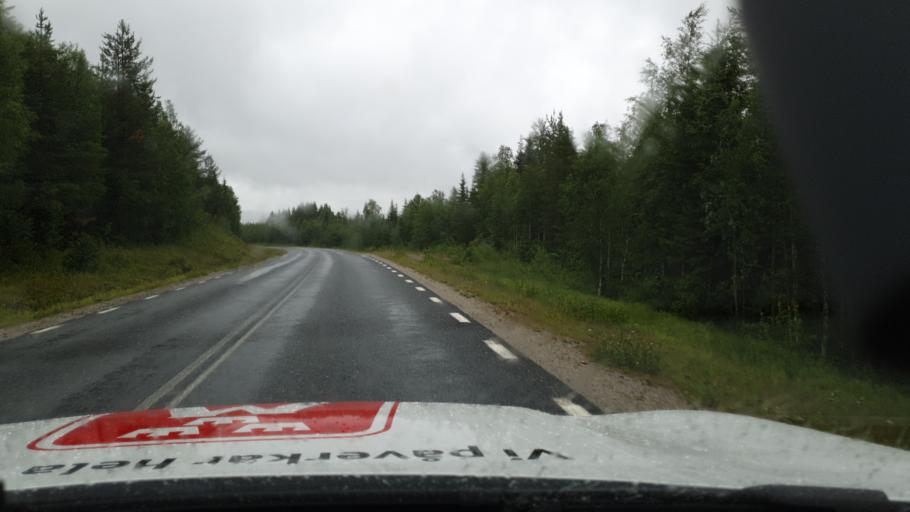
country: SE
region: Vaesterbotten
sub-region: Lycksele Kommun
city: Lycksele
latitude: 64.4924
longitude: 18.2890
